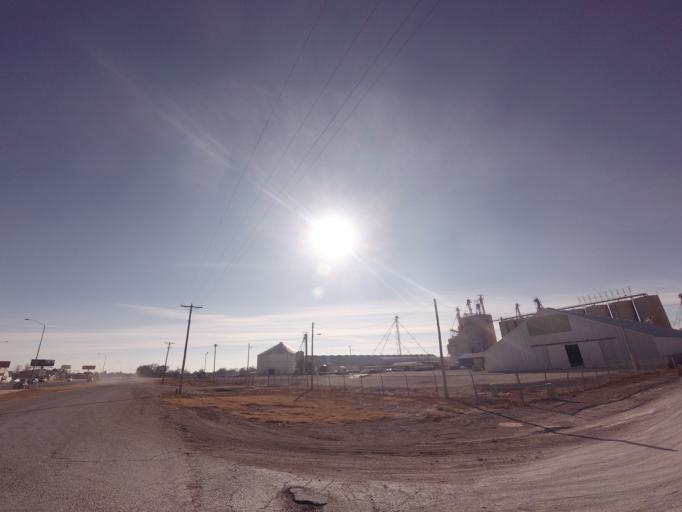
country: US
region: New Mexico
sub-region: Curry County
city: Clovis
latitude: 34.3948
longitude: -103.1968
